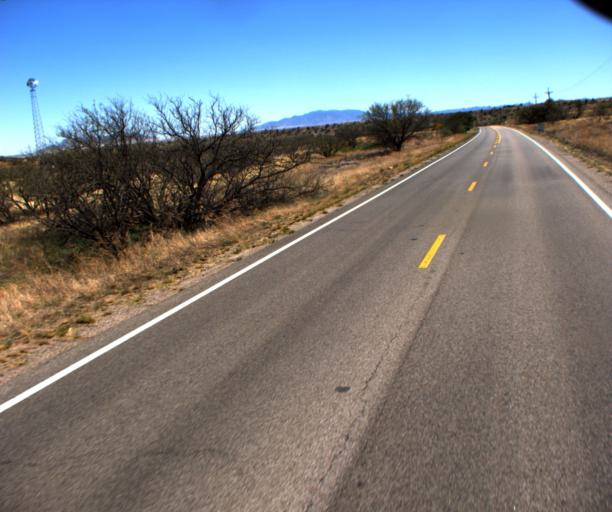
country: US
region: Arizona
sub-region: Pima County
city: Corona de Tucson
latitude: 31.7896
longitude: -110.6989
